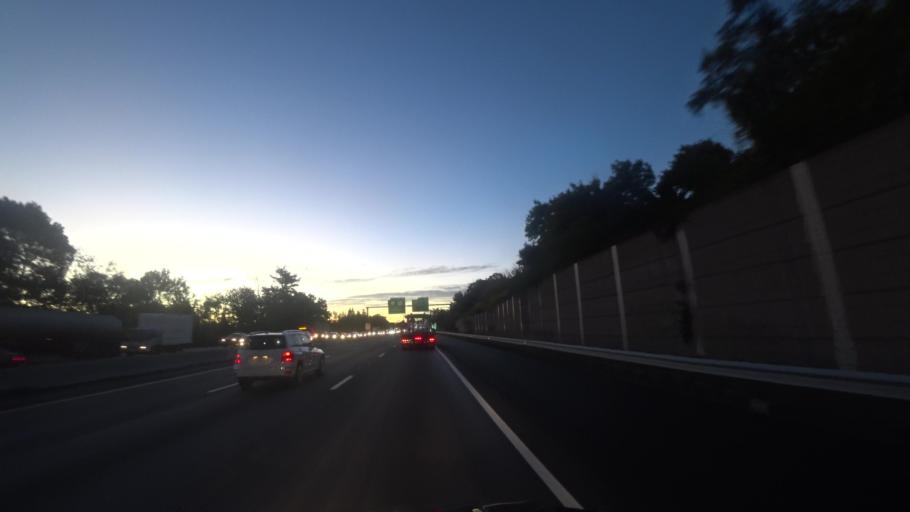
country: US
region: Massachusetts
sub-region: Essex County
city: Lynnfield
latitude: 42.5179
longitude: -71.0511
